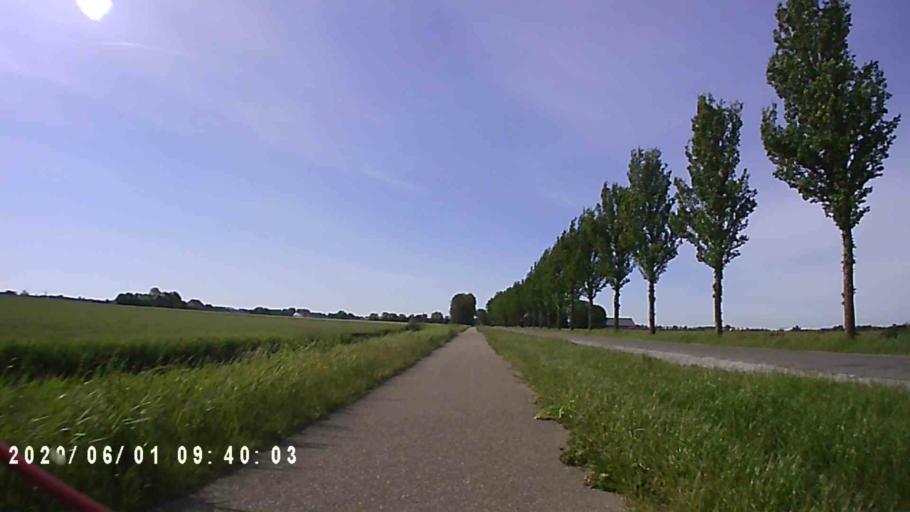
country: NL
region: Friesland
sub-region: Menameradiel
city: Berltsum
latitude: 53.2535
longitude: 5.6811
